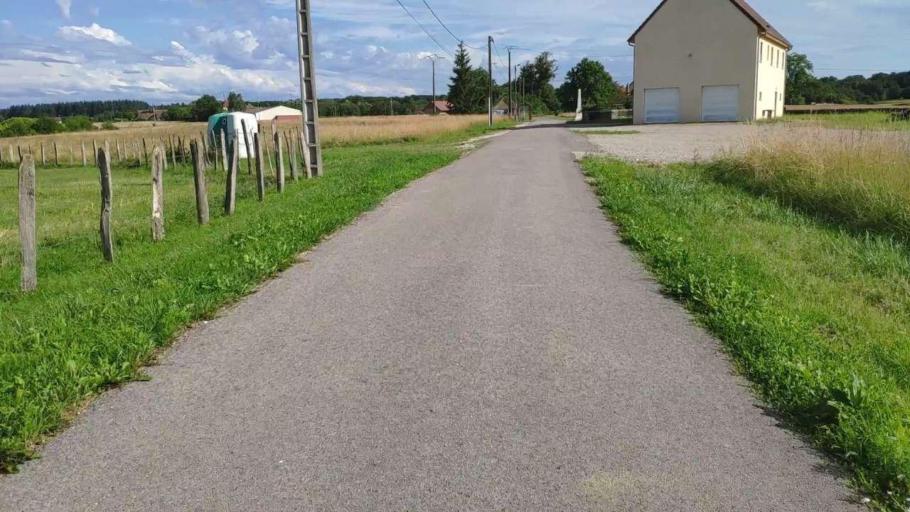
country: FR
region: Franche-Comte
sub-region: Departement du Jura
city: Bletterans
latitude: 46.8095
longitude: 5.5060
